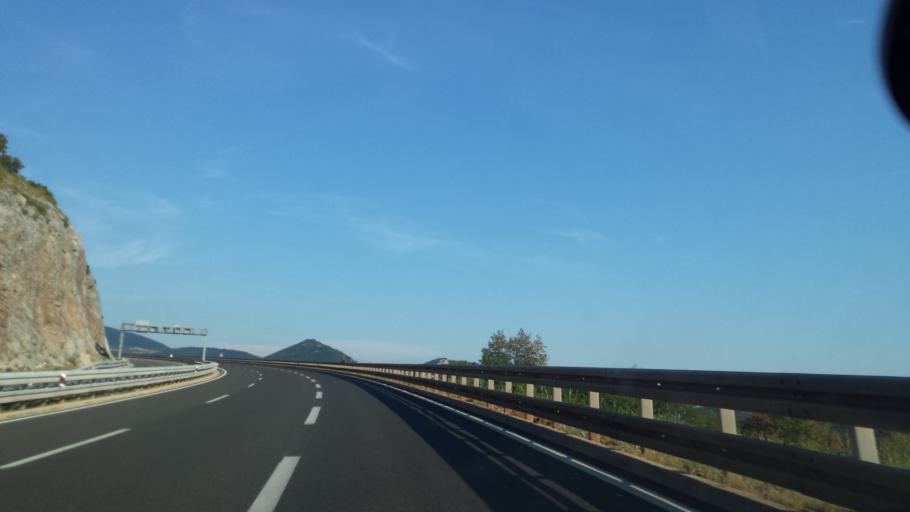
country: HR
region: Primorsko-Goranska
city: Skrljevo
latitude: 45.3642
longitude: 14.5512
